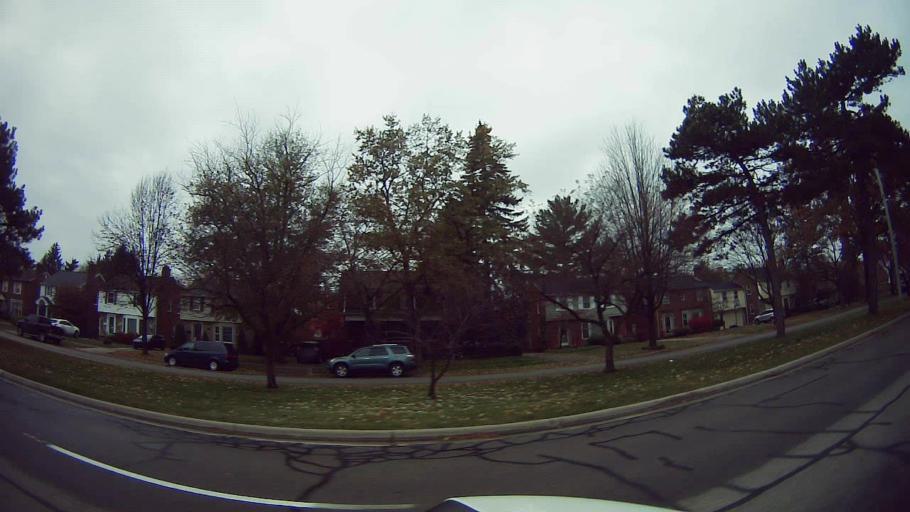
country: US
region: Michigan
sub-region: Wayne County
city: Dearborn Heights
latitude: 42.3130
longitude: -83.2538
